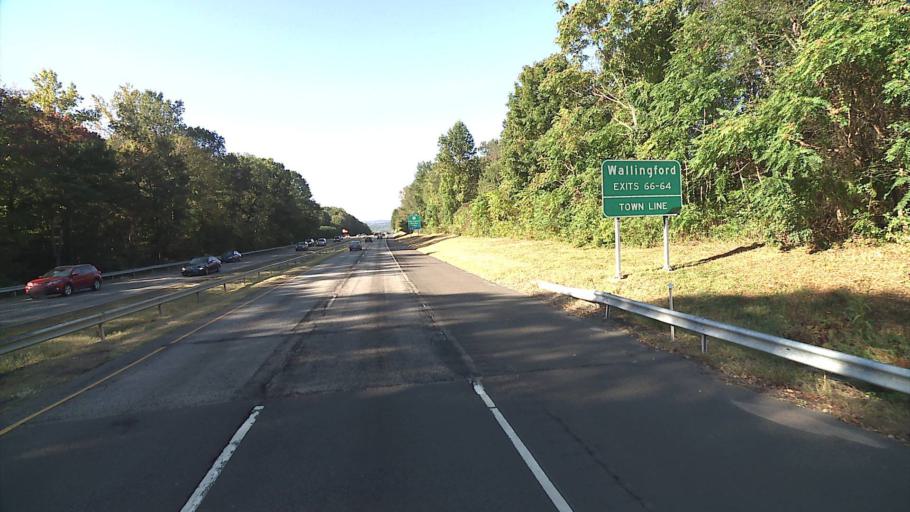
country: US
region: Connecticut
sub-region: New Haven County
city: Meriden
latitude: 41.5037
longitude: -72.7926
